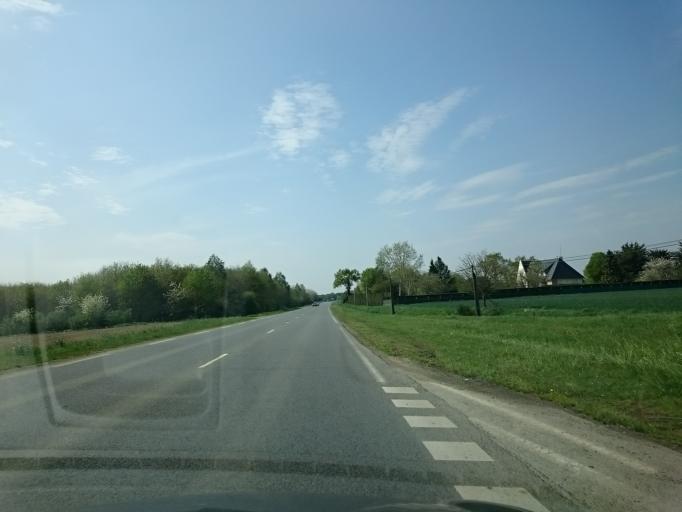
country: FR
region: Brittany
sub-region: Departement d'Ille-et-Vilaine
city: Chantepie
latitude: 48.0766
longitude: -1.5877
